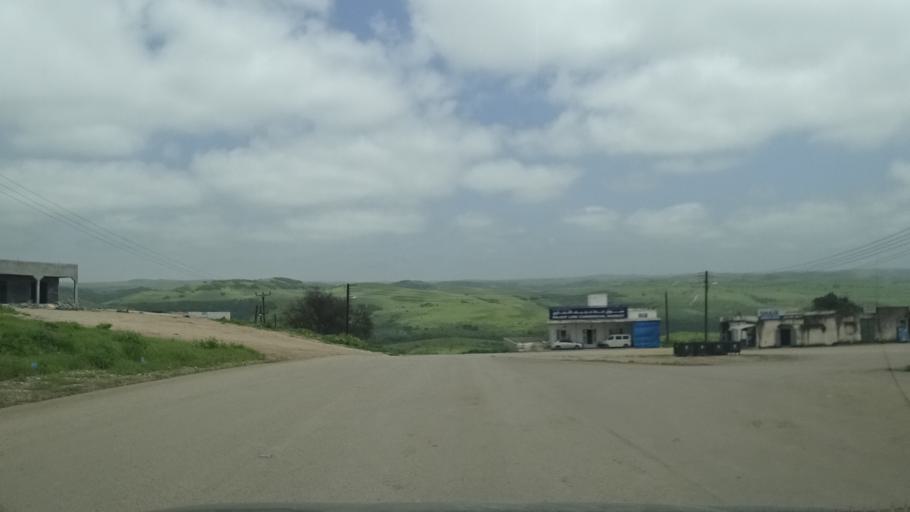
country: OM
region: Zufar
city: Salalah
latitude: 17.1926
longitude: 54.1654
